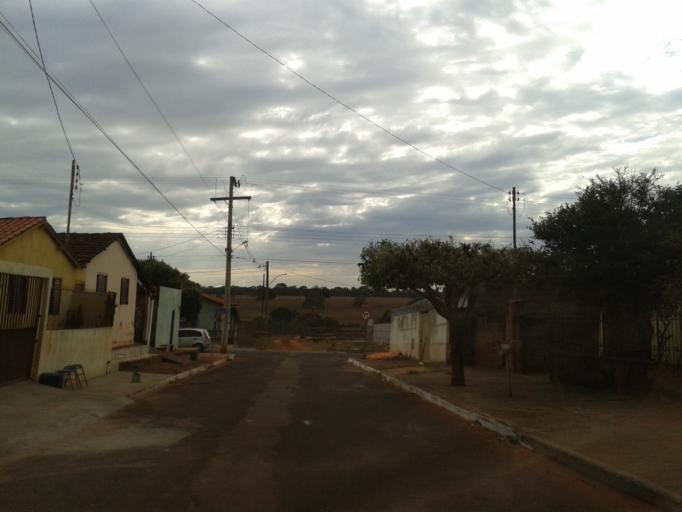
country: BR
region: Minas Gerais
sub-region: Santa Vitoria
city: Santa Vitoria
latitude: -18.8356
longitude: -50.1320
